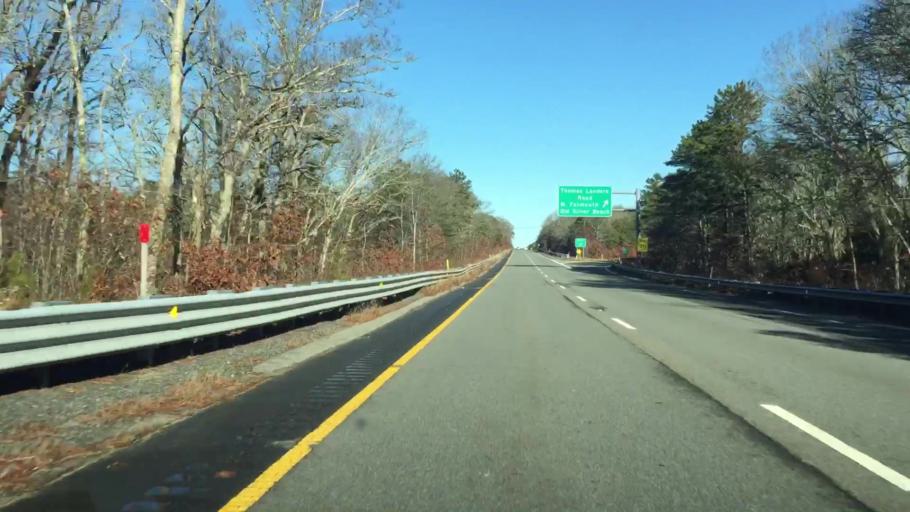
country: US
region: Massachusetts
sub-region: Barnstable County
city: West Falmouth
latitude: 41.6134
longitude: -70.6219
